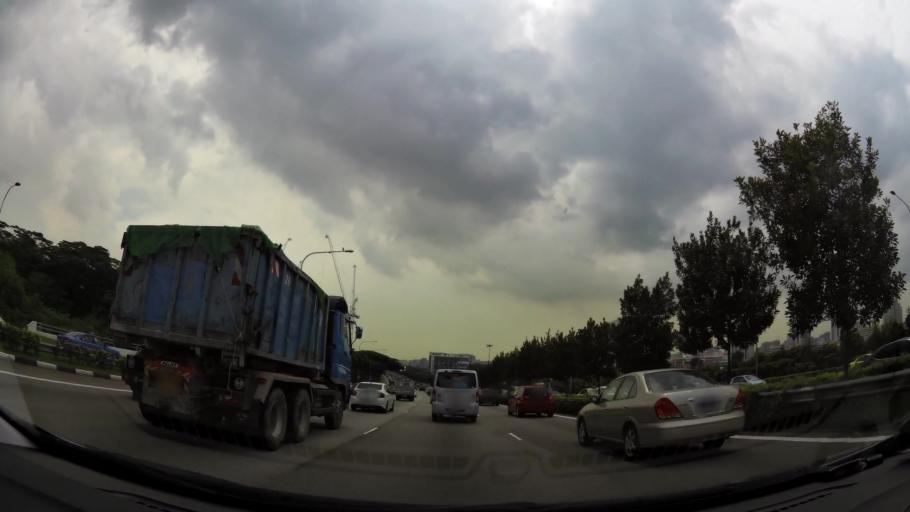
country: SG
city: Singapore
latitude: 1.3533
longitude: 103.8571
